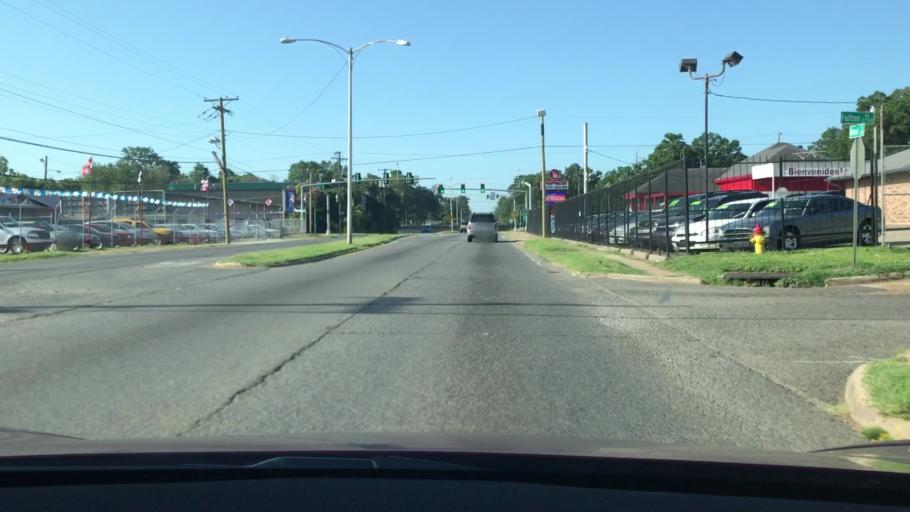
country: US
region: Louisiana
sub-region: Caddo Parish
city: Shreveport
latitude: 32.4719
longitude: -93.7801
